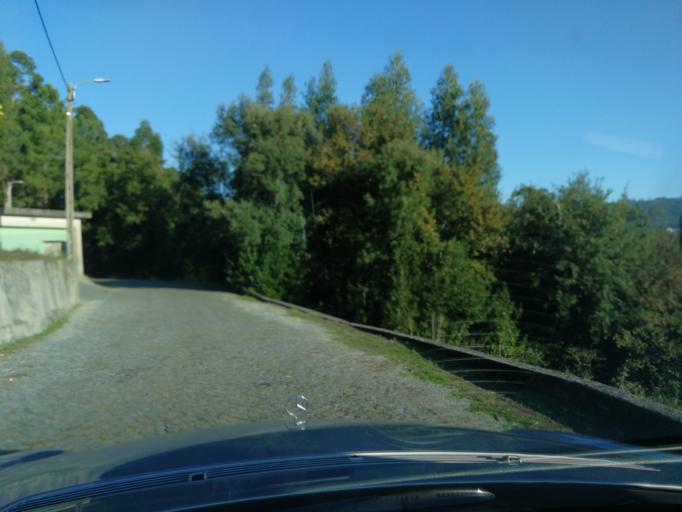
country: PT
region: Braga
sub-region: Braga
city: Oliveira
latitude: 41.4540
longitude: -8.4650
